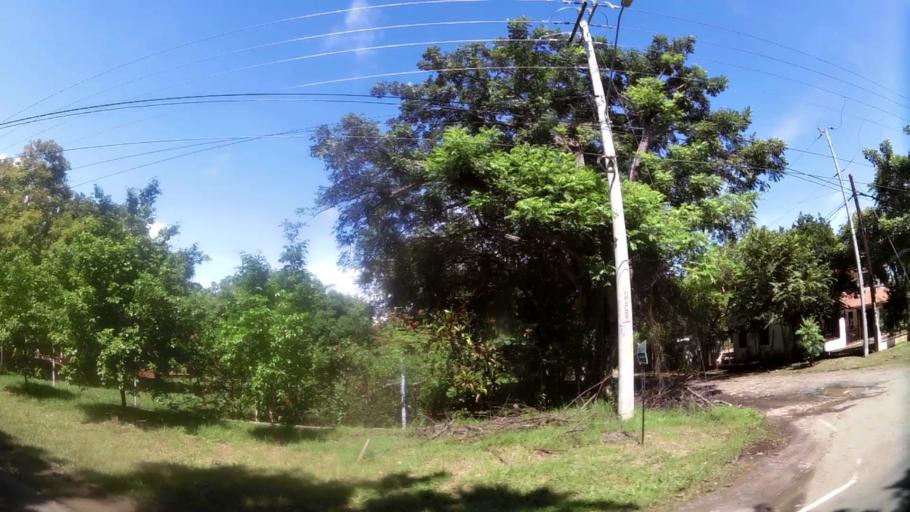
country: PA
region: Panama
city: Nueva Gorgona
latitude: 8.5592
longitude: -79.8790
